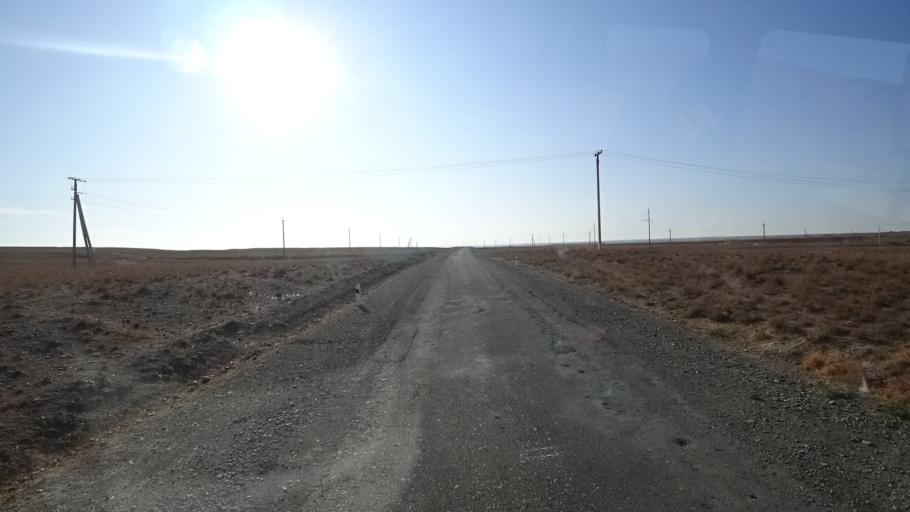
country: UZ
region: Navoiy
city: Beshrabot
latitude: 40.2321
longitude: 65.4150
